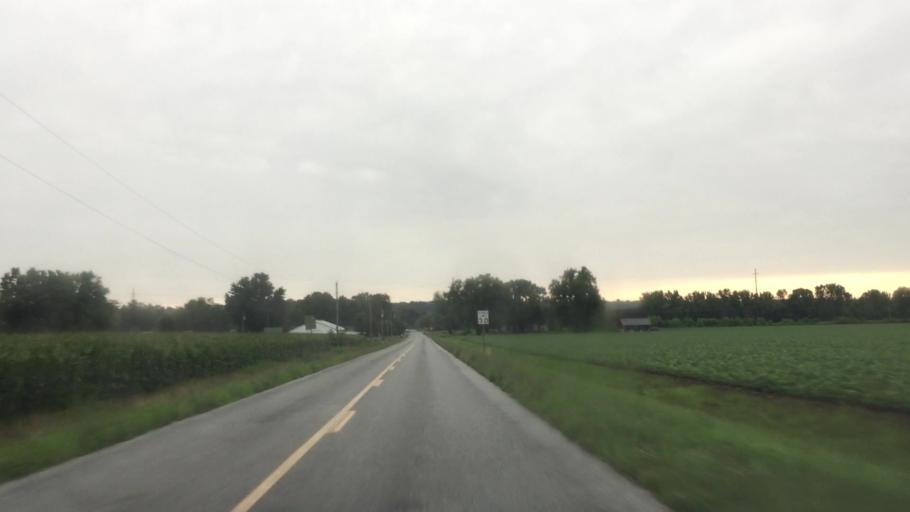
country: US
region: Iowa
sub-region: Lee County
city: Fort Madison
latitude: 40.6137
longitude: -91.2819
